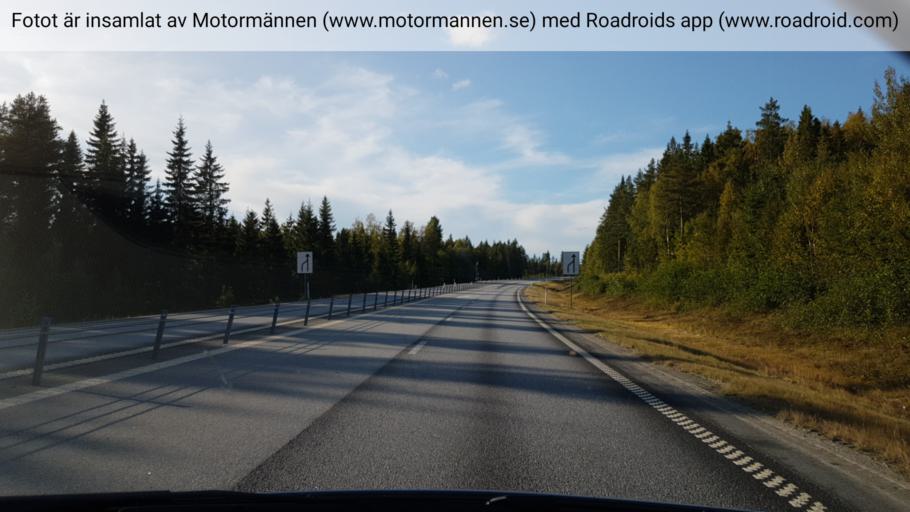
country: SE
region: Vaesterbotten
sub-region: Vannas Kommun
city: Vannasby
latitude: 63.9009
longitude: 19.9008
